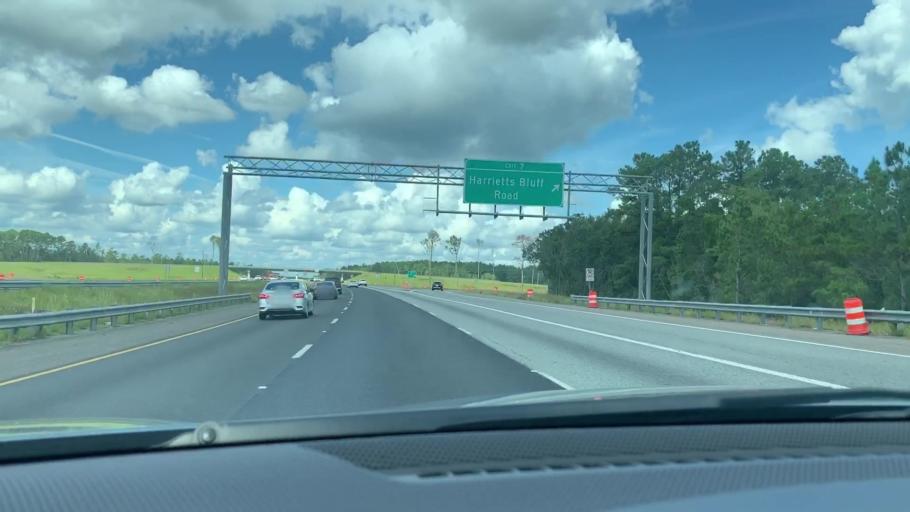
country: US
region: Georgia
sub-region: Camden County
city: Kingsland
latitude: 30.8426
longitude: -81.6703
